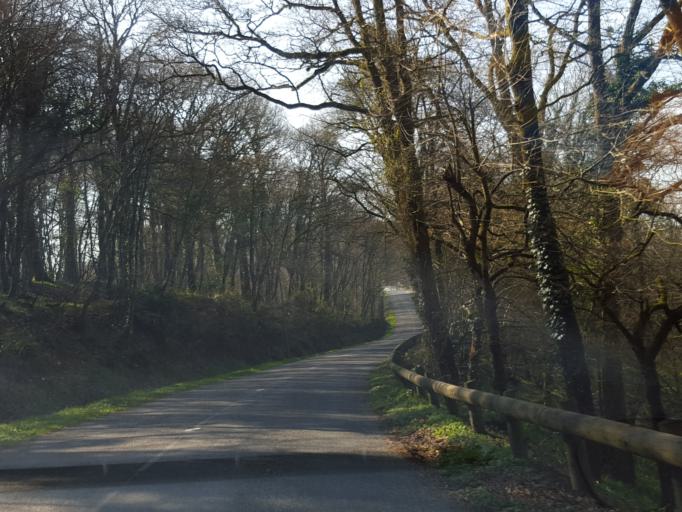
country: FR
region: Pays de la Loire
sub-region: Departement de la Vendee
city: Chavagnes-en-Paillers
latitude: 46.8632
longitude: -1.2517
